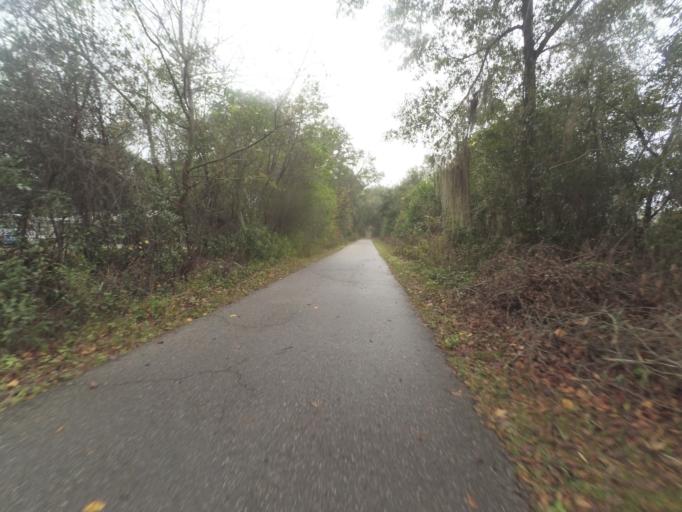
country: US
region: Florida
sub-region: Alachua County
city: Hawthorne
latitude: 29.5875
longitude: -82.0924
